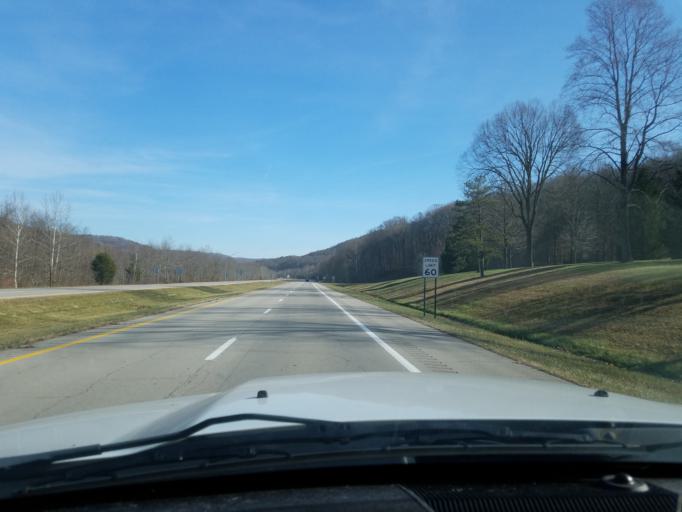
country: US
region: Ohio
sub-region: Adams County
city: Peebles
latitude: 39.0425
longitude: -83.2285
